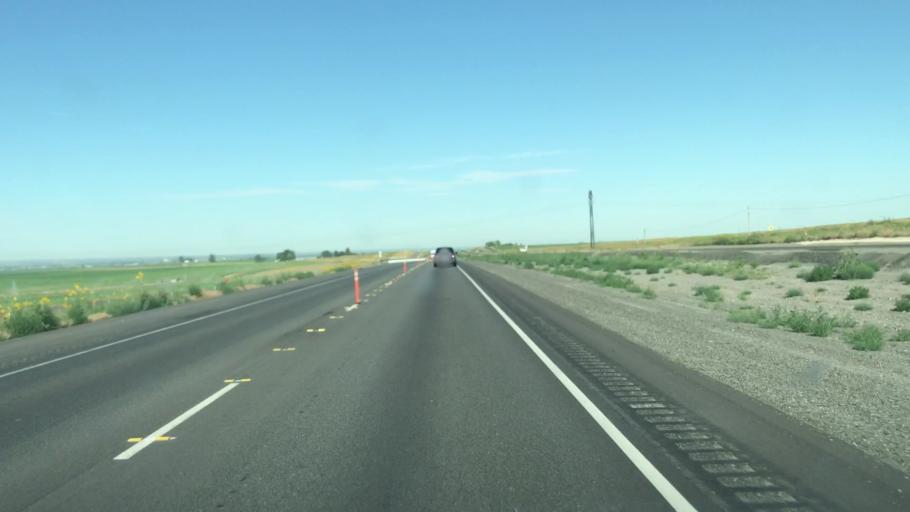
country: US
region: Idaho
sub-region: Twin Falls County
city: Hansen
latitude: 42.5761
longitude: -114.2339
